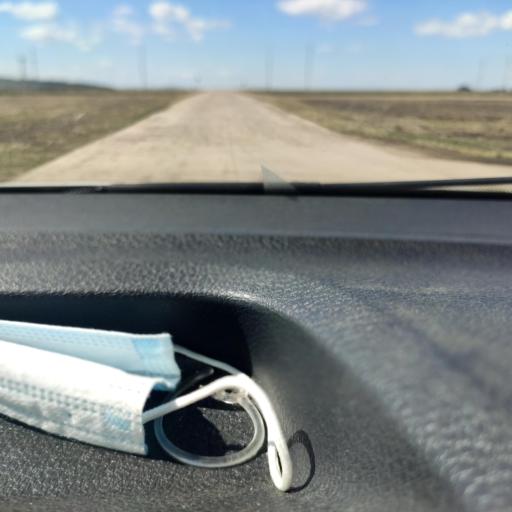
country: RU
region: Bashkortostan
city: Alekseyevka
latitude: 54.7907
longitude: 55.1793
